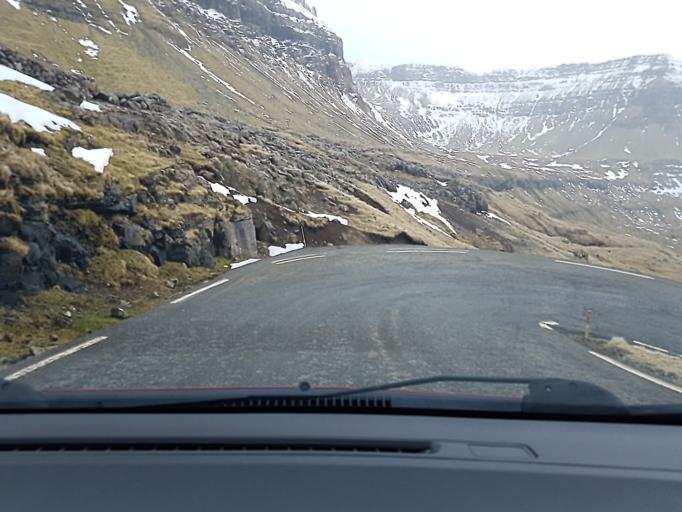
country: FO
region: Streymoy
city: Kollafjordhur
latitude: 62.0501
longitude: -6.9221
